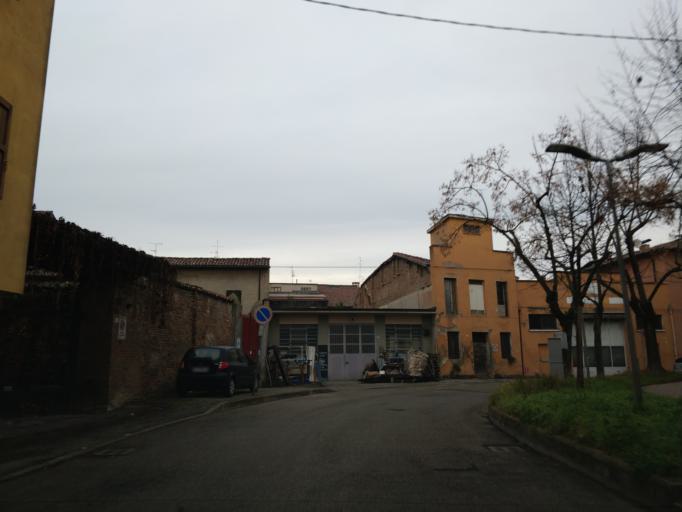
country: IT
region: Emilia-Romagna
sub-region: Provincia di Ferrara
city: Cento
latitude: 44.7252
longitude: 11.2923
